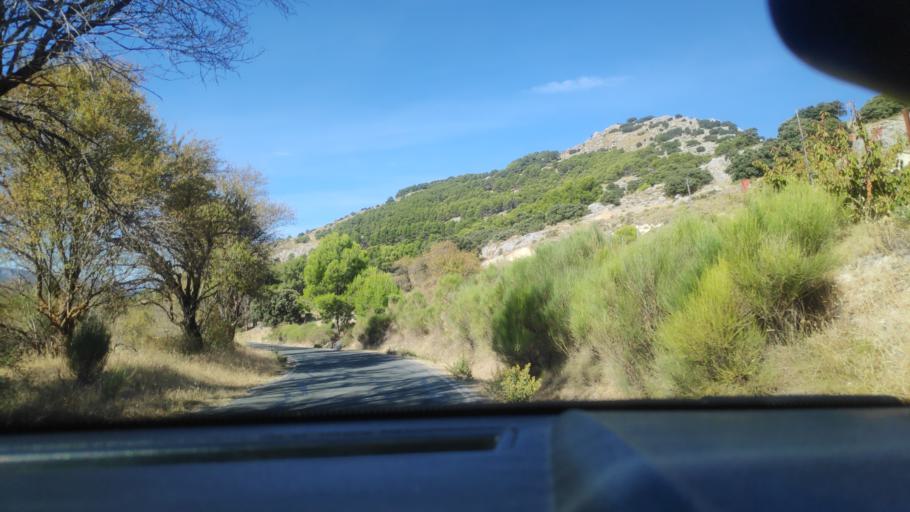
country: ES
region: Andalusia
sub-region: Provincia de Jaen
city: Torres
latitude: 37.7870
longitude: -3.4857
